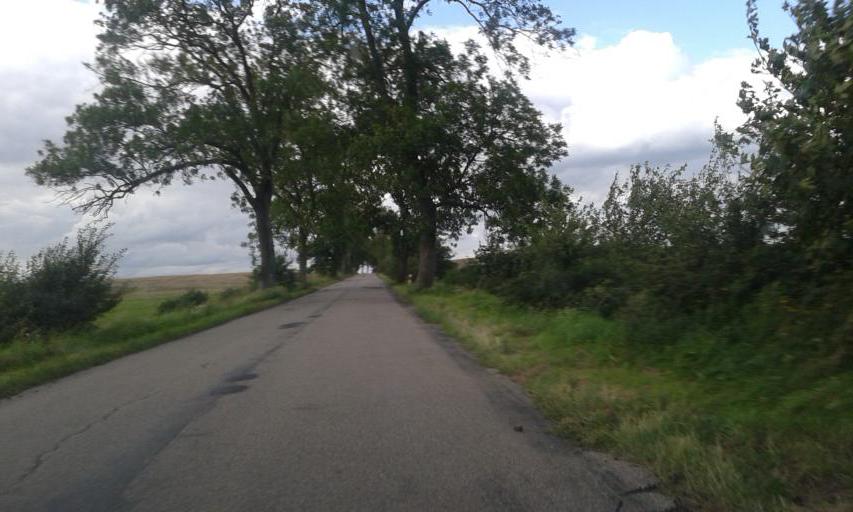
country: PL
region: West Pomeranian Voivodeship
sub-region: Powiat szczecinecki
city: Barwice
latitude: 53.7216
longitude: 16.3546
